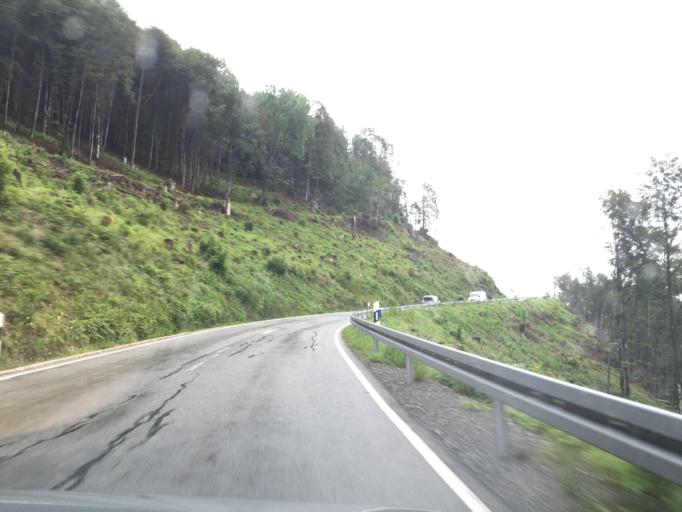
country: DE
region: Baden-Wuerttemberg
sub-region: Freiburg Region
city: Todtnau
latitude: 47.8490
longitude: 7.9254
